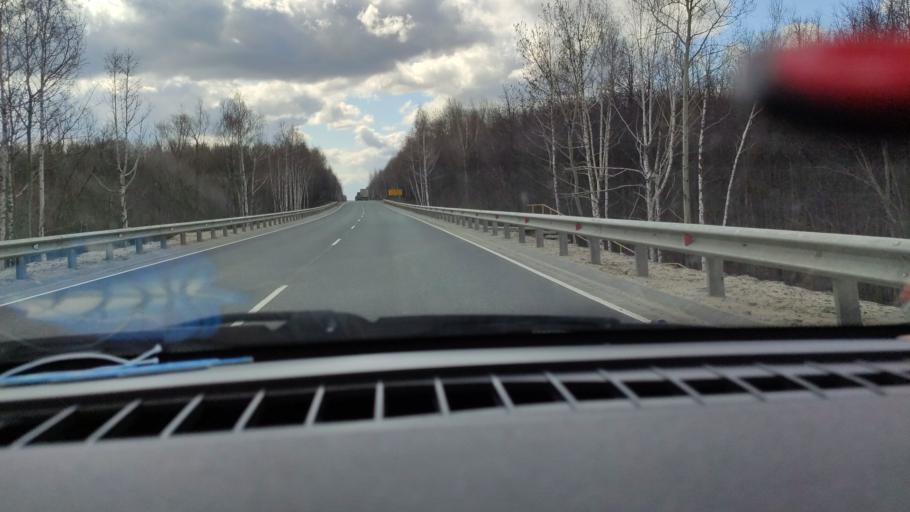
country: RU
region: Saratov
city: Khvalynsk
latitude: 52.4380
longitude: 48.0097
